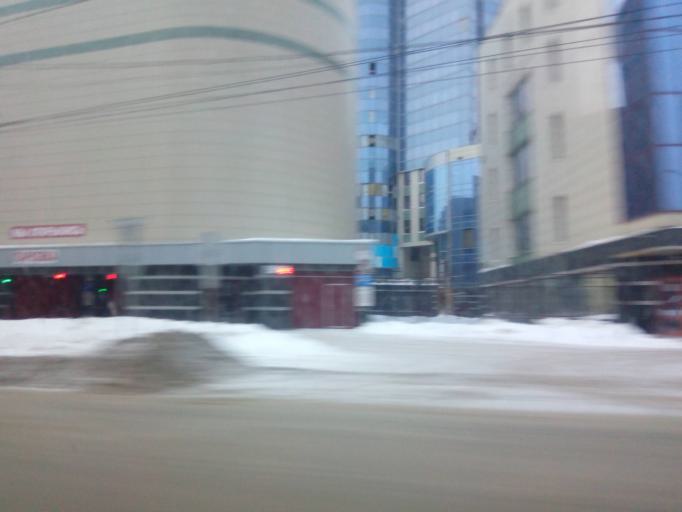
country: RU
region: Novosibirsk
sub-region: Novosibirskiy Rayon
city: Novosibirsk
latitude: 55.0282
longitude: 82.9061
